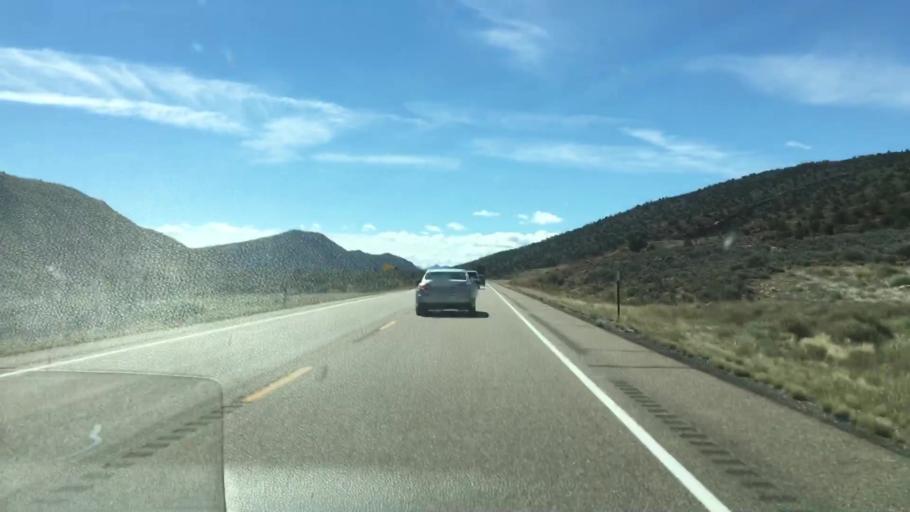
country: US
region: Utah
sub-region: Kane County
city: Kanab
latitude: 37.1376
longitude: -111.9752
